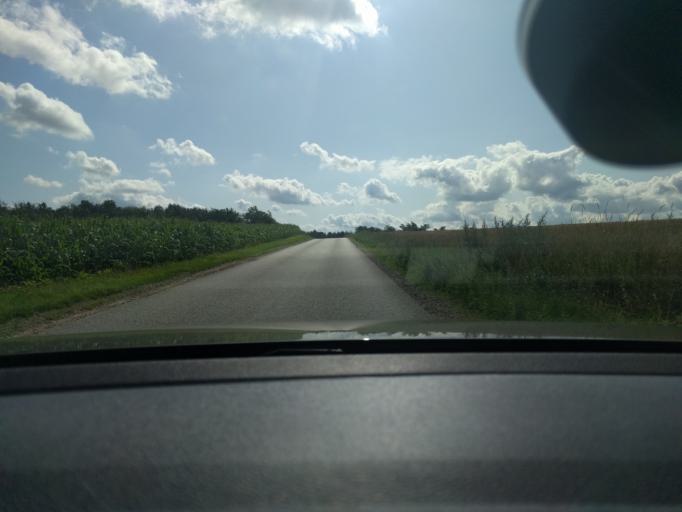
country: DK
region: Central Jutland
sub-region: Viborg Kommune
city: Viborg
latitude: 56.5236
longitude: 9.3794
